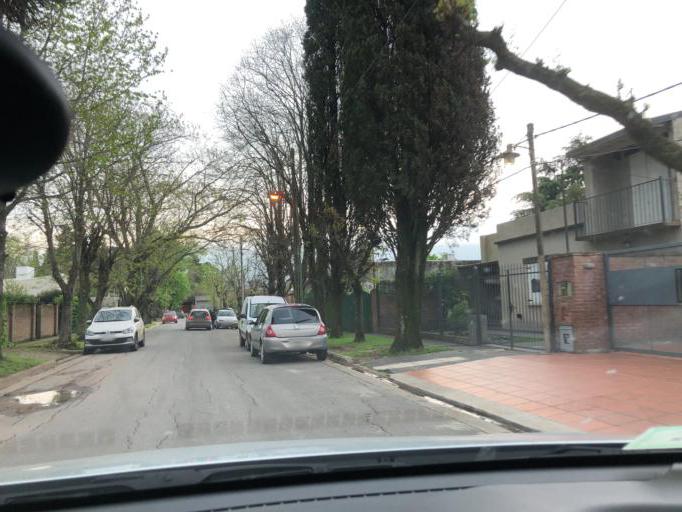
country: AR
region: Buenos Aires
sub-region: Partido de La Plata
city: La Plata
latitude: -34.8769
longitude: -58.0451
